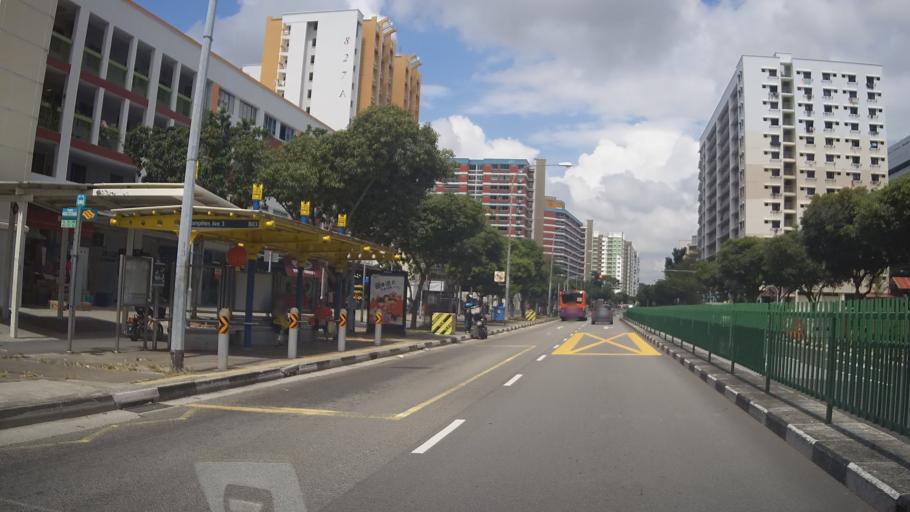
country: SG
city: Singapore
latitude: 1.3498
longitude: 103.9343
